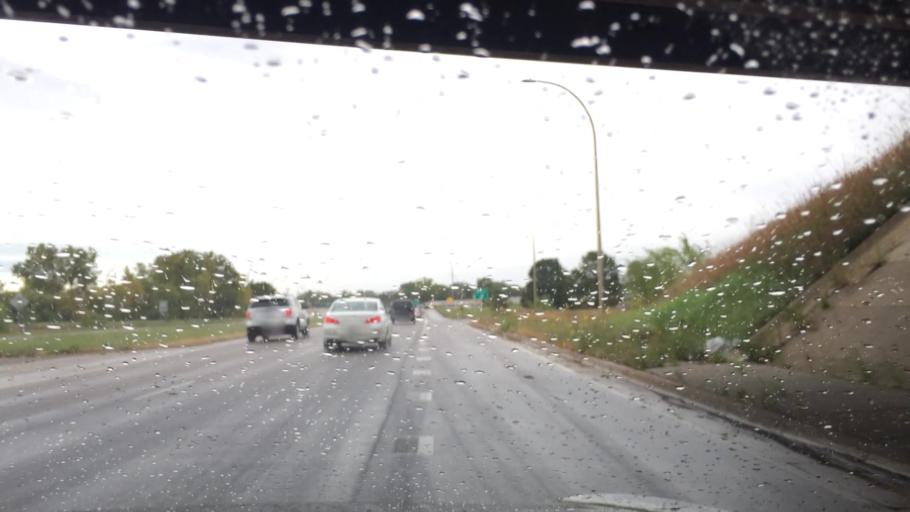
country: US
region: Minnesota
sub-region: Anoka County
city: Spring Lake Park
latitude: 45.1206
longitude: -93.2374
